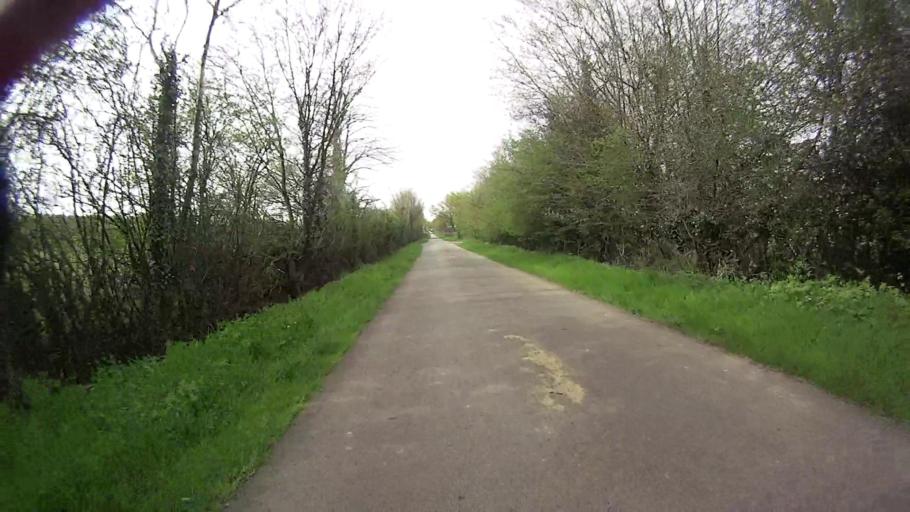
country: GB
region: England
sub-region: West Sussex
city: Gossops Green
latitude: 51.1380
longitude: -0.2368
